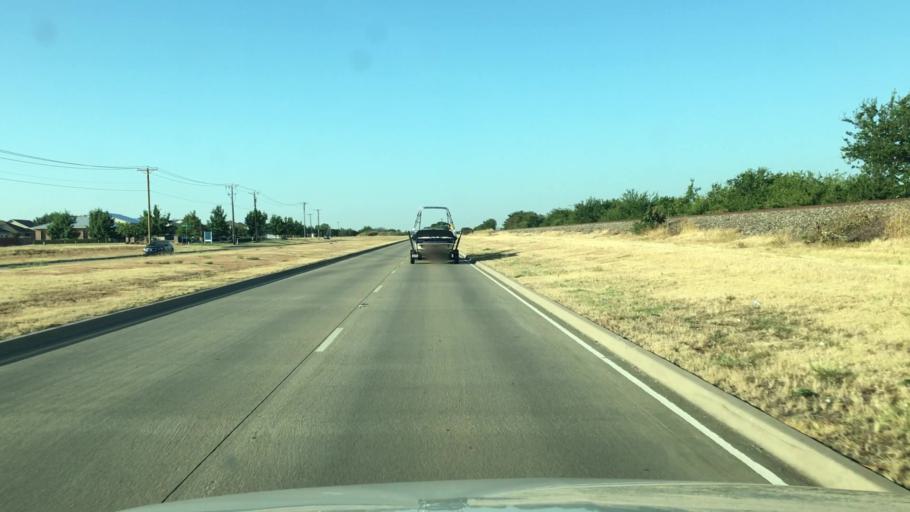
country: US
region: Texas
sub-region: Tarrant County
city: Crowley
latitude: 32.5486
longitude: -97.3654
